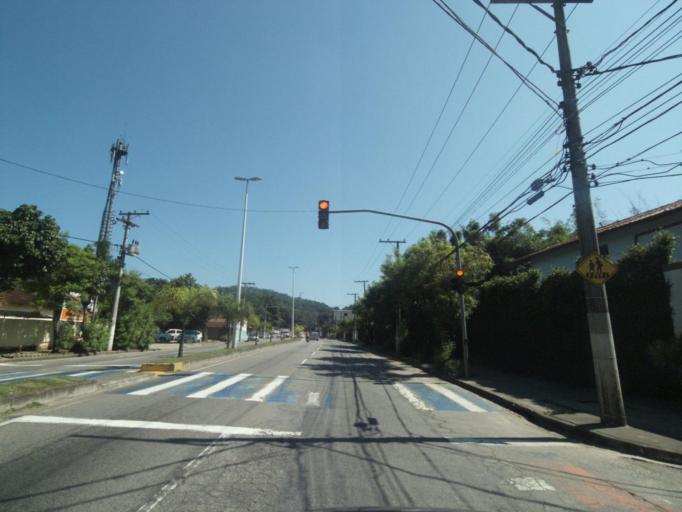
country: BR
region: Rio de Janeiro
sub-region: Niteroi
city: Niteroi
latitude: -22.8968
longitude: -43.0393
